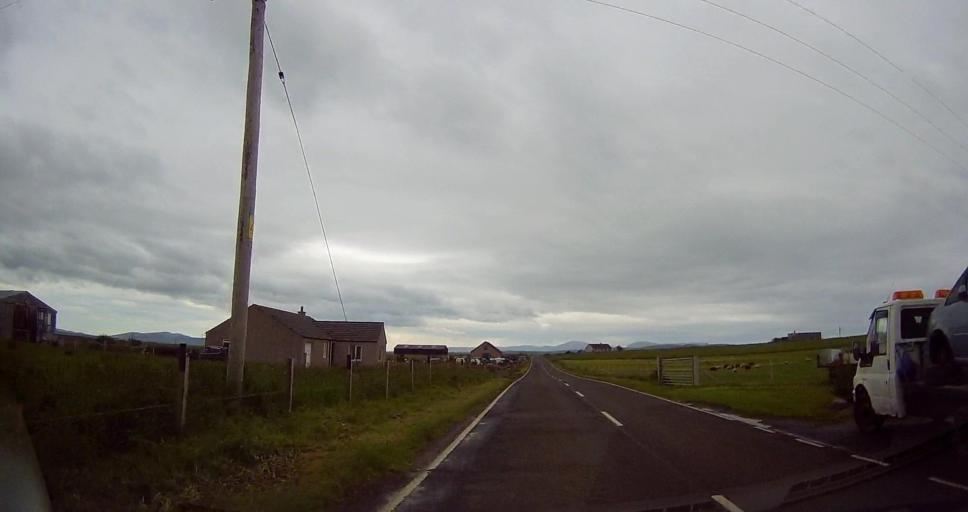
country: GB
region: Scotland
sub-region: Orkney Islands
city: Stromness
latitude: 59.0790
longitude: -3.2774
